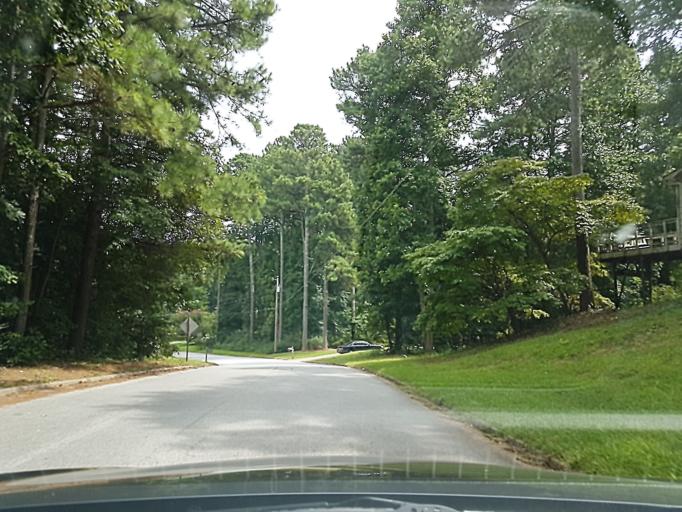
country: US
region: Georgia
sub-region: Douglas County
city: Douglasville
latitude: 33.6925
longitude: -84.7134
